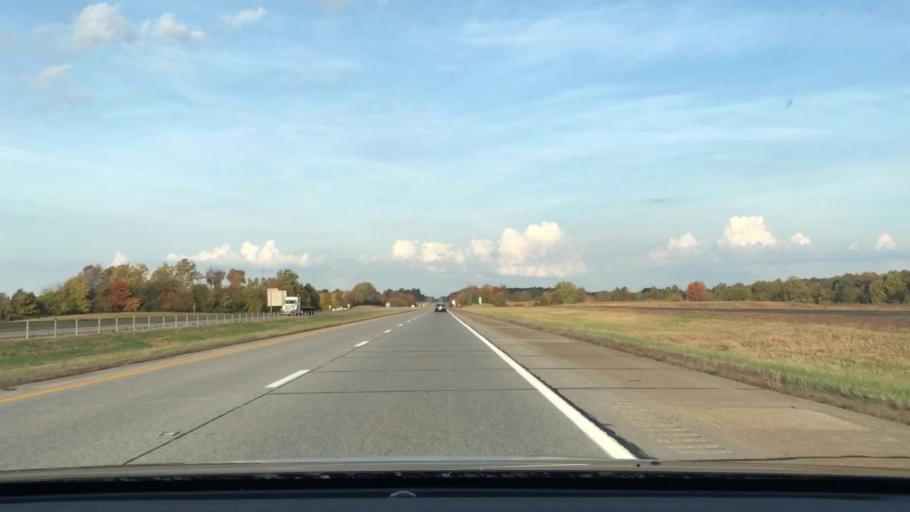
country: US
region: Kentucky
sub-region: Trigg County
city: Cadiz
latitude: 36.9765
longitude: -87.9002
